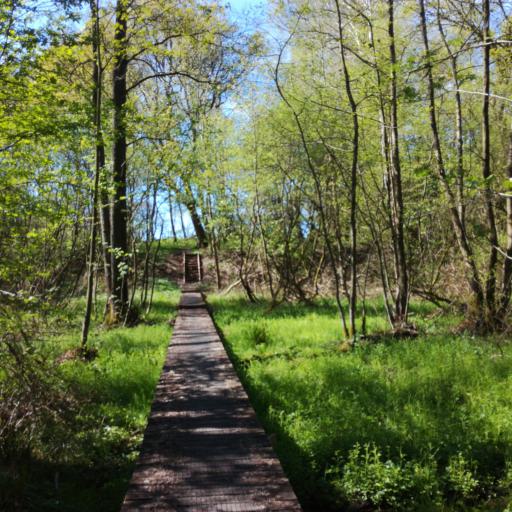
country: DK
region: South Denmark
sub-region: Vejle Kommune
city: Brejning
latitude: 55.6123
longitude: 9.6974
